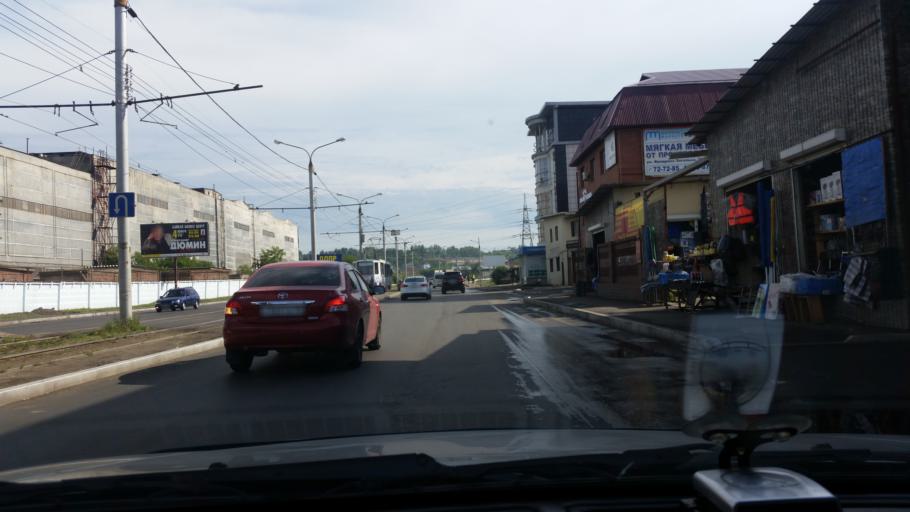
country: RU
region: Irkutsk
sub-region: Irkutskiy Rayon
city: Irkutsk
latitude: 52.2893
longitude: 104.3080
